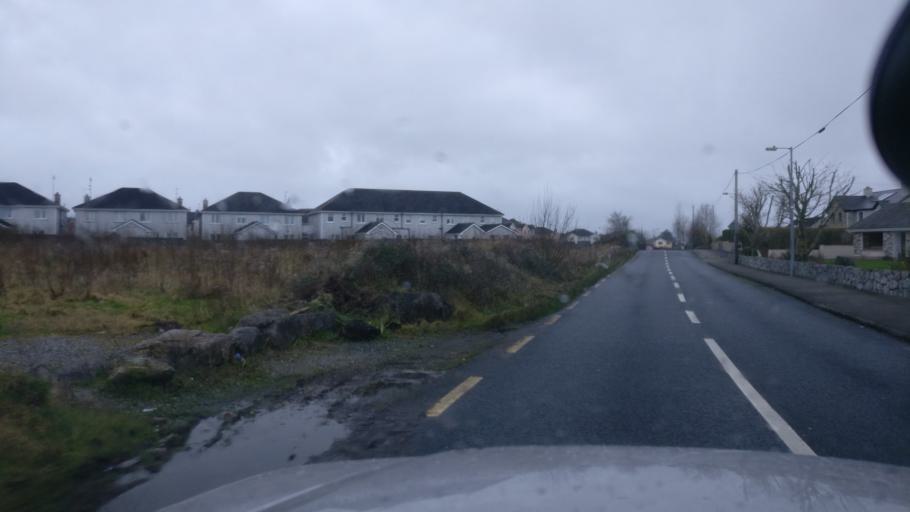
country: IE
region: Connaught
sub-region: County Galway
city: Loughrea
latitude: 53.2060
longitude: -8.5569
